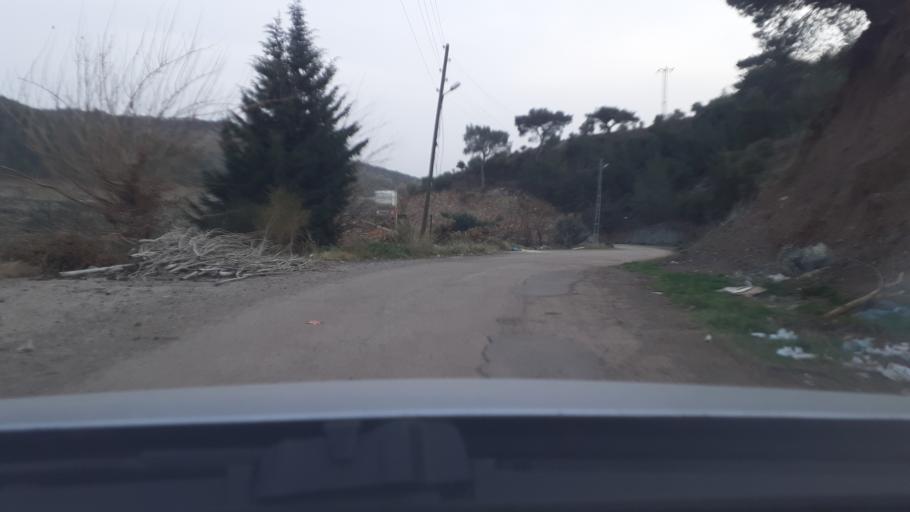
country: TR
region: Hatay
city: Kirikhan
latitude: 36.5328
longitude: 36.3148
